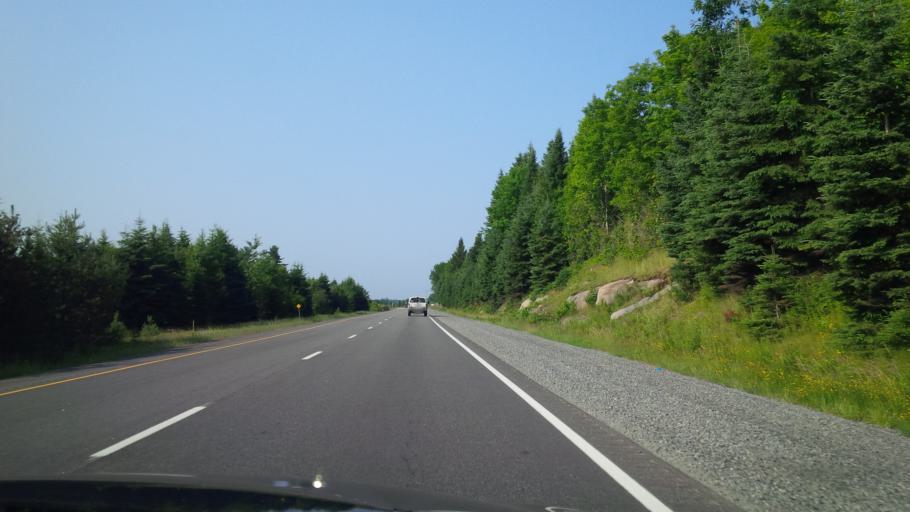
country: CA
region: Ontario
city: Huntsville
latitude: 45.2800
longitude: -79.2777
